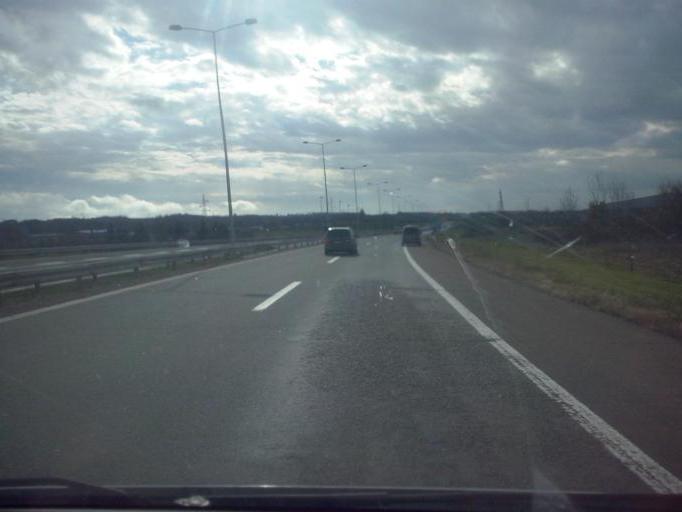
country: RS
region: Central Serbia
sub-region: Pomoravski Okrug
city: Paracin
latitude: 43.8622
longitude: 21.4377
